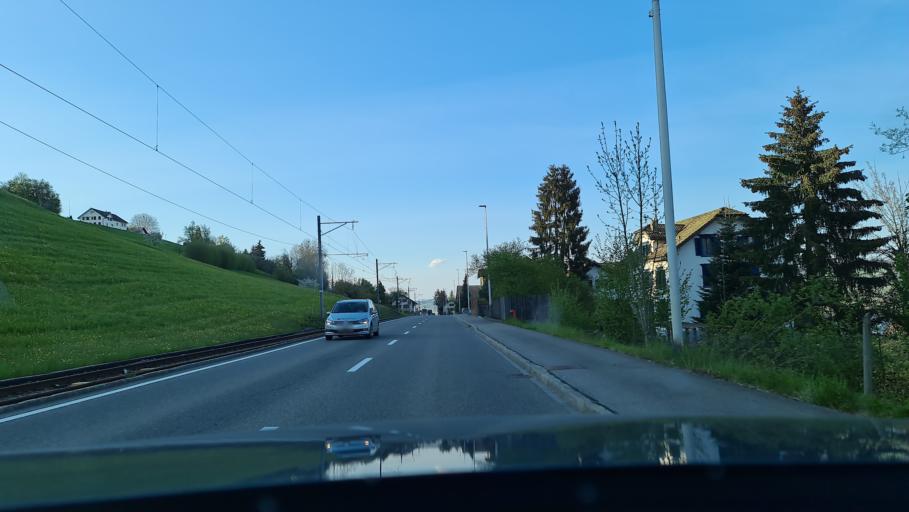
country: CH
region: Aargau
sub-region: Bezirk Lenzburg
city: Boniswil
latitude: 47.2939
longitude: 8.1986
